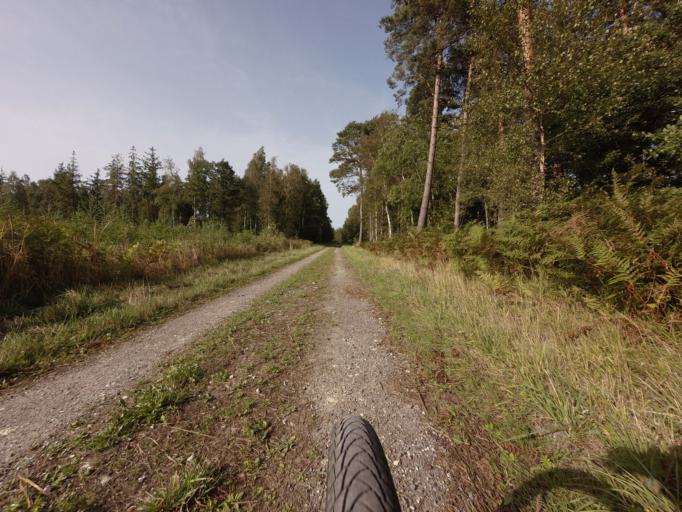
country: DK
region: Zealand
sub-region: Vordingborg Kommune
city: Praesto
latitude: 55.1494
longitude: 12.0994
